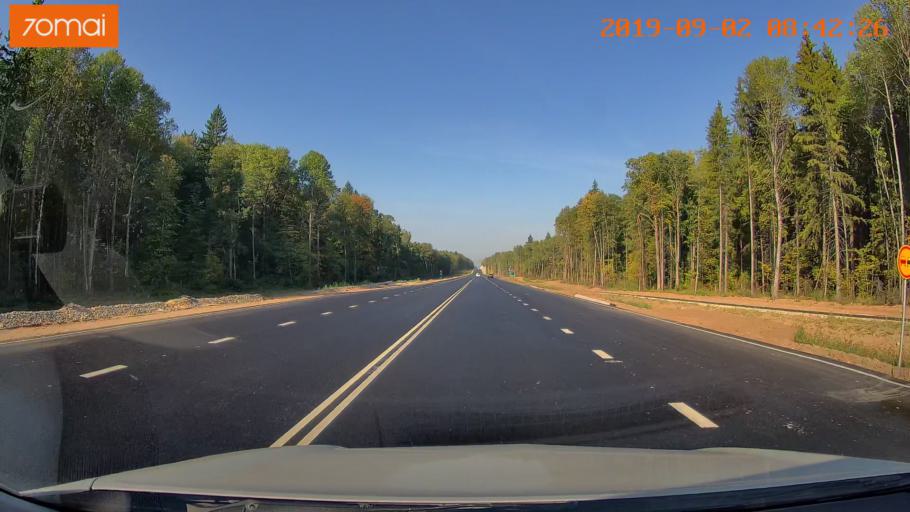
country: RU
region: Kaluga
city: Kudinovo
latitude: 54.9725
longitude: 36.0868
